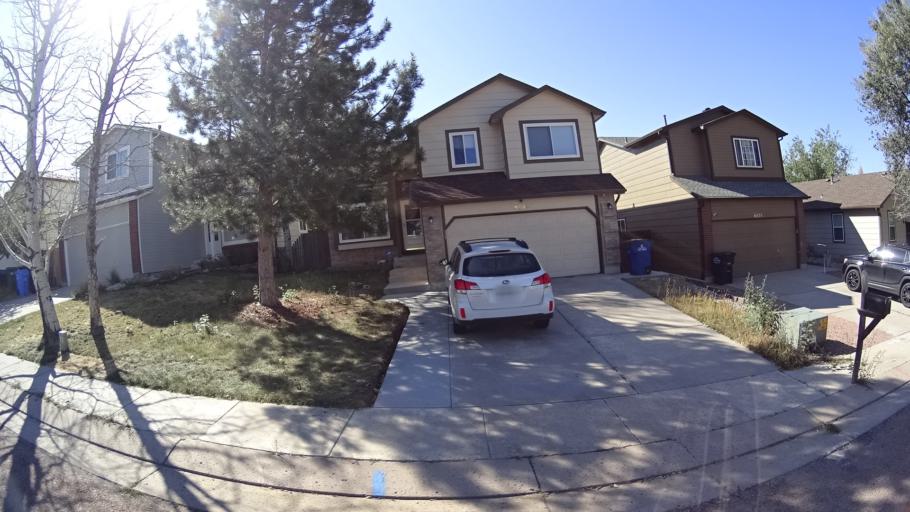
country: US
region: Colorado
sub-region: El Paso County
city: Cimarron Hills
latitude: 38.8713
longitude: -104.7082
